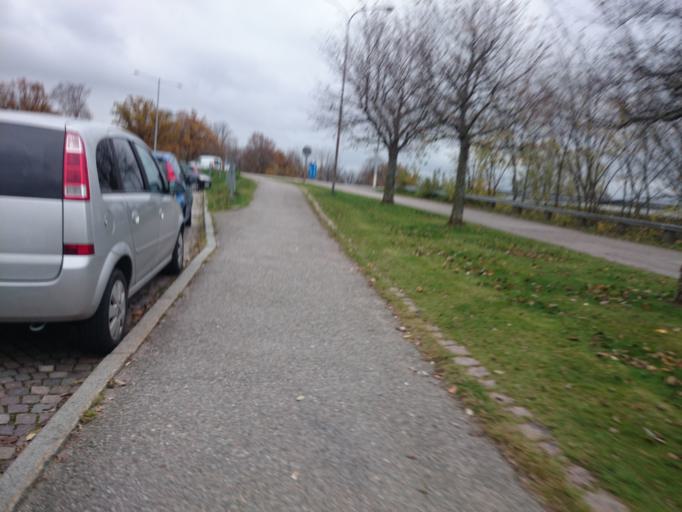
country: SE
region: Soedermanland
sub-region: Nykopings Kommun
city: Nykoping
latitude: 58.7508
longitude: 16.9982
